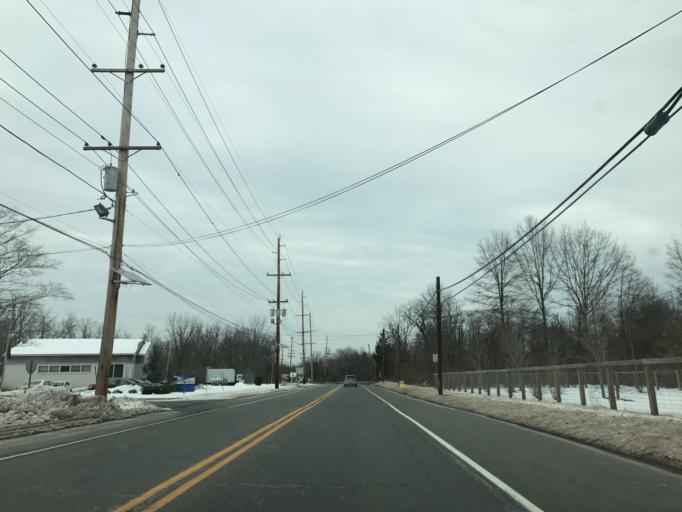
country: US
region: New Jersey
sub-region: Somerset County
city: Bloomingdale
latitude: 40.4689
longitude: -74.6613
